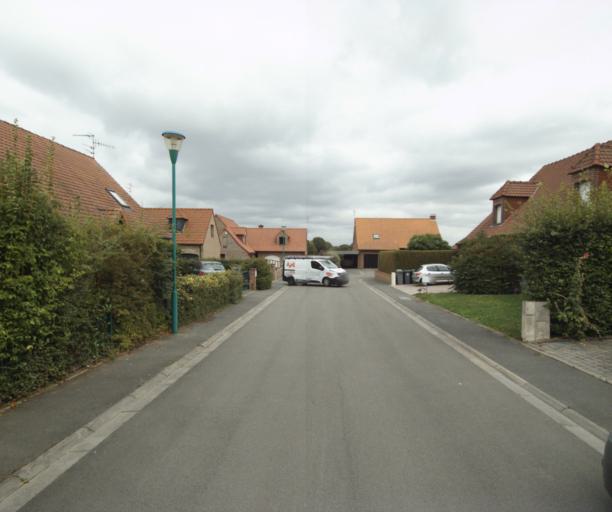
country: FR
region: Nord-Pas-de-Calais
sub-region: Departement du Nord
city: Lesquin
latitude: 50.5923
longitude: 3.1219
